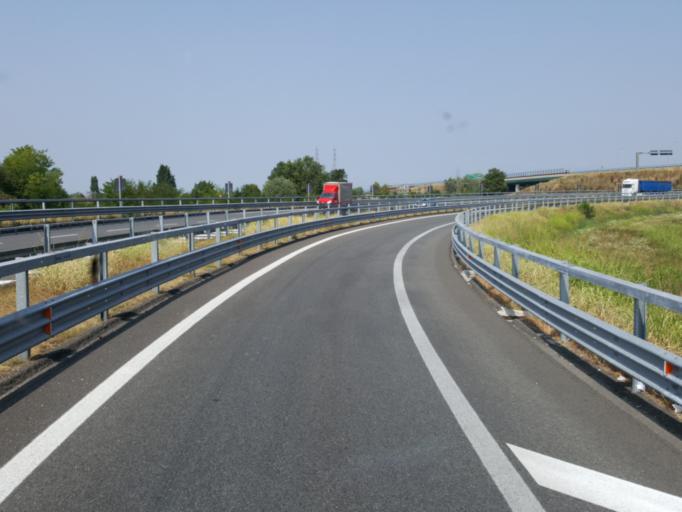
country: IT
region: Lombardy
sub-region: Citta metropolitana di Milano
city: Pozzuolo Martesana
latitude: 45.5013
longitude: 9.4421
